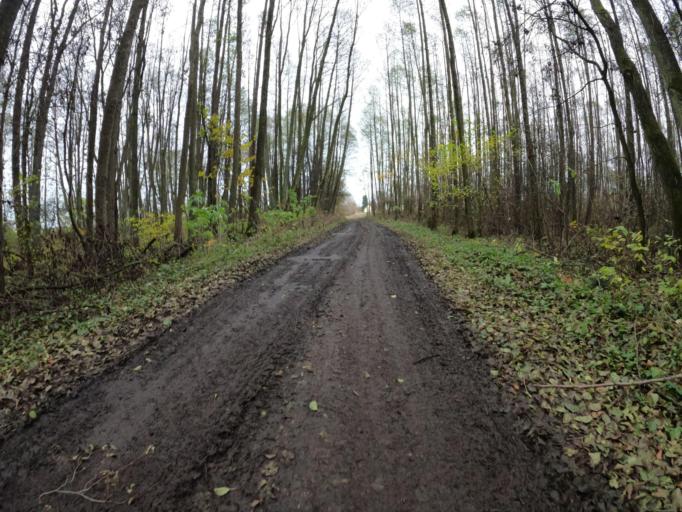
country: PL
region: West Pomeranian Voivodeship
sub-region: Powiat walecki
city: Miroslawiec
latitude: 53.2897
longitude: 16.1438
